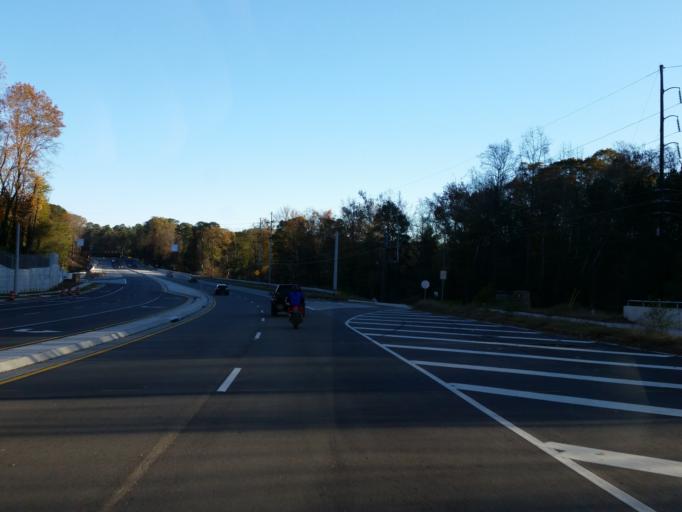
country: US
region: Georgia
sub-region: Cobb County
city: Vinings
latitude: 33.8705
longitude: -84.4562
